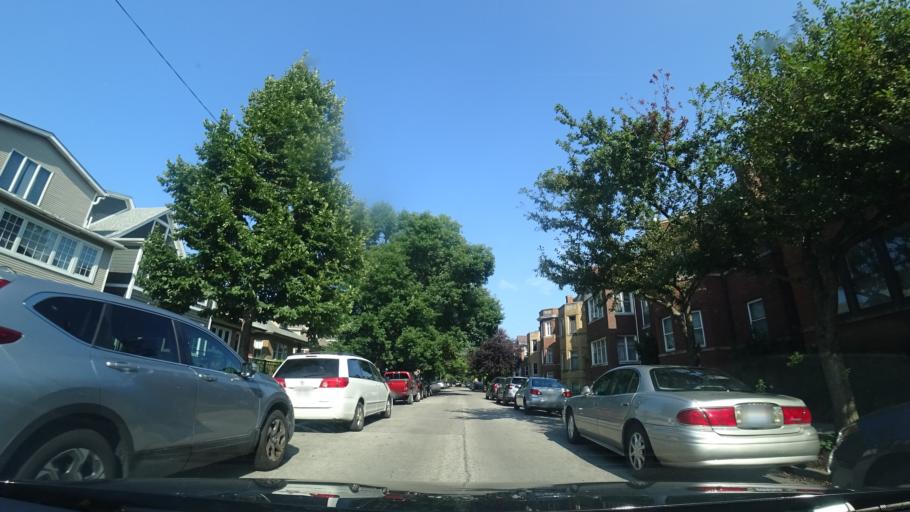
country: US
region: Illinois
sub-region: Cook County
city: Lincolnwood
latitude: 41.9731
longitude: -87.6861
